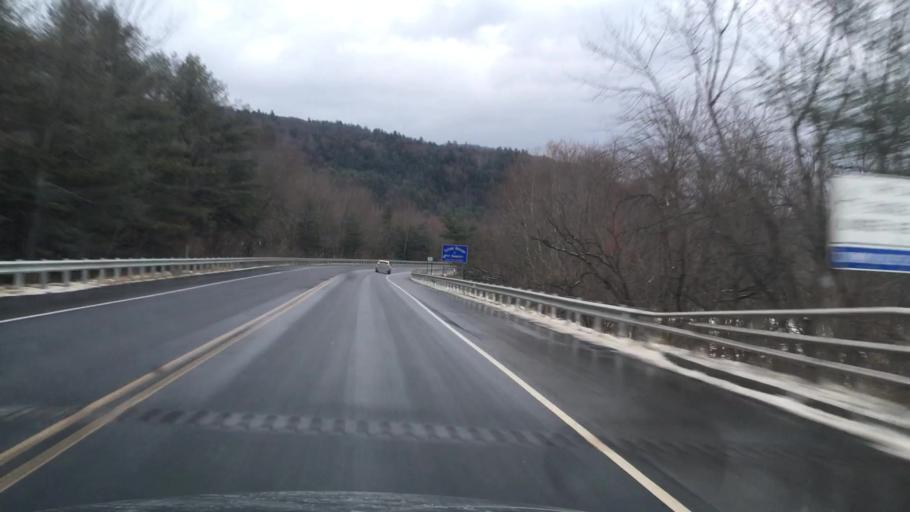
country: US
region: New Hampshire
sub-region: Sullivan County
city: Claremont
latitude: 43.4029
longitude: -72.3990
